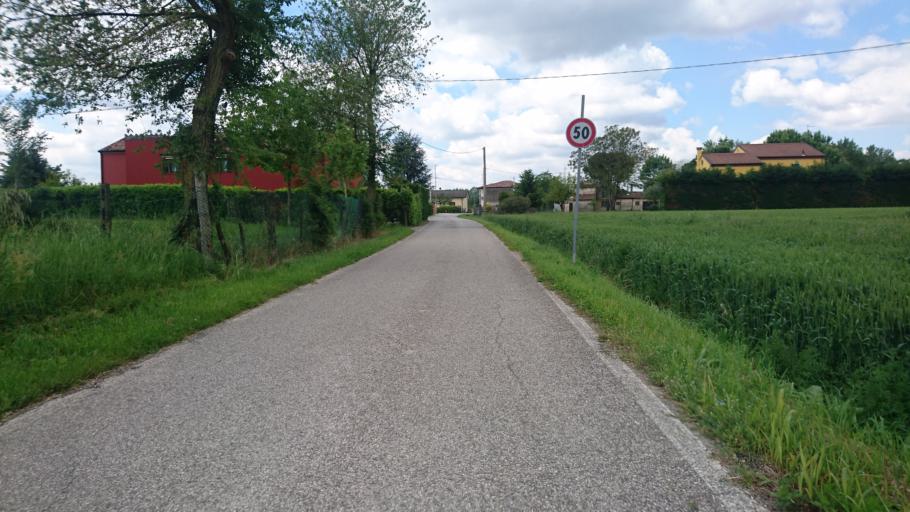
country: IT
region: Veneto
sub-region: Provincia di Padova
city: Villa Estense
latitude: 45.1566
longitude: 11.6515
